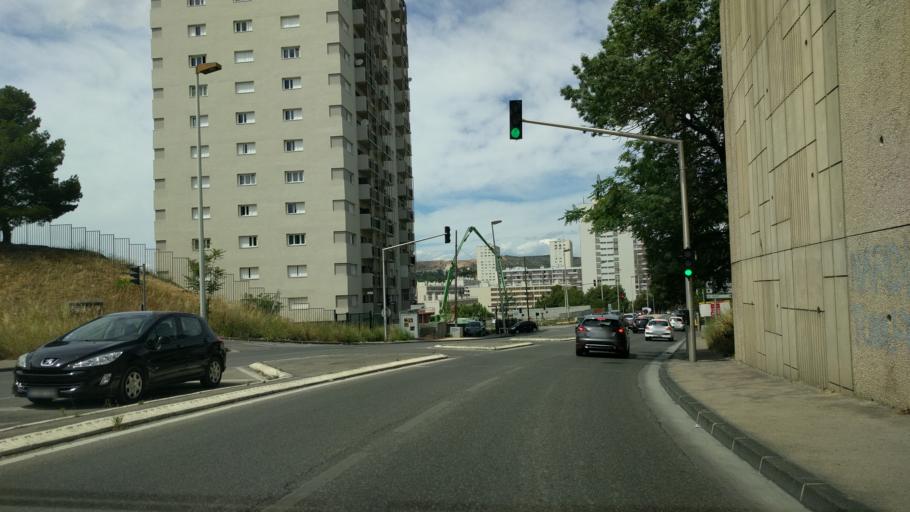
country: FR
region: Provence-Alpes-Cote d'Azur
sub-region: Departement des Bouches-du-Rhone
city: Marseille 13
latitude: 43.3288
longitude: 5.3979
